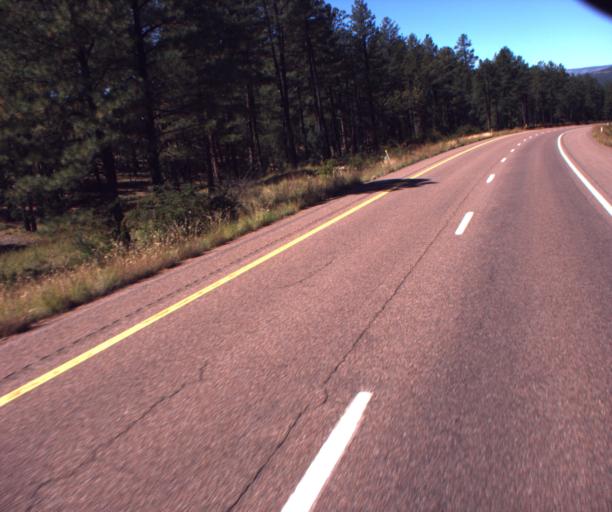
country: US
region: Arizona
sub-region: Gila County
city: Star Valley
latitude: 34.2968
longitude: -110.9835
